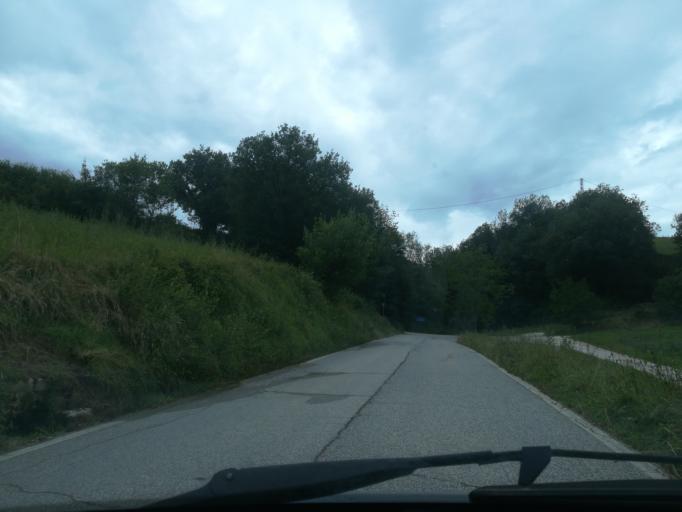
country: IT
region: The Marches
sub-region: Province of Fermo
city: Montefortino
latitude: 42.9340
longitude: 13.3734
